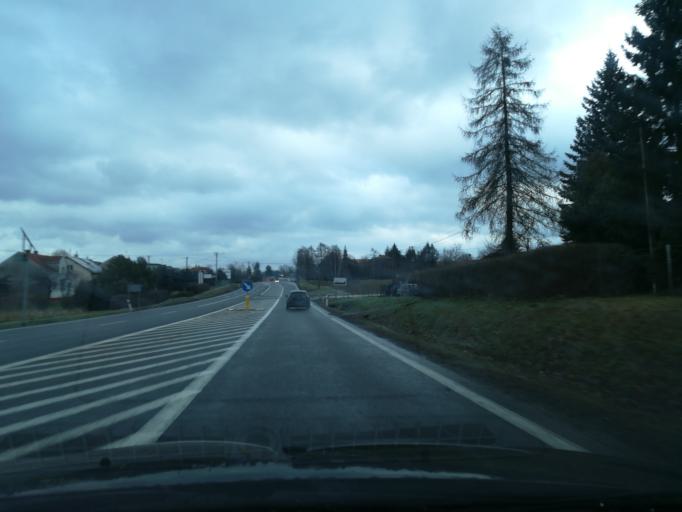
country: PL
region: Subcarpathian Voivodeship
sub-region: Powiat lancucki
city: Kosina
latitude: 50.0728
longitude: 22.3207
